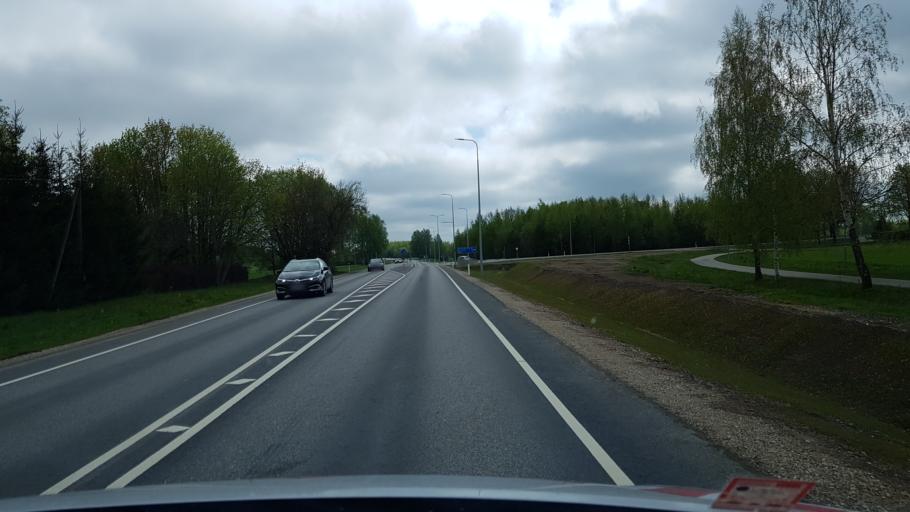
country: EE
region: Viljandimaa
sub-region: Viljandi linn
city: Viljandi
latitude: 58.2425
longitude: 25.5942
